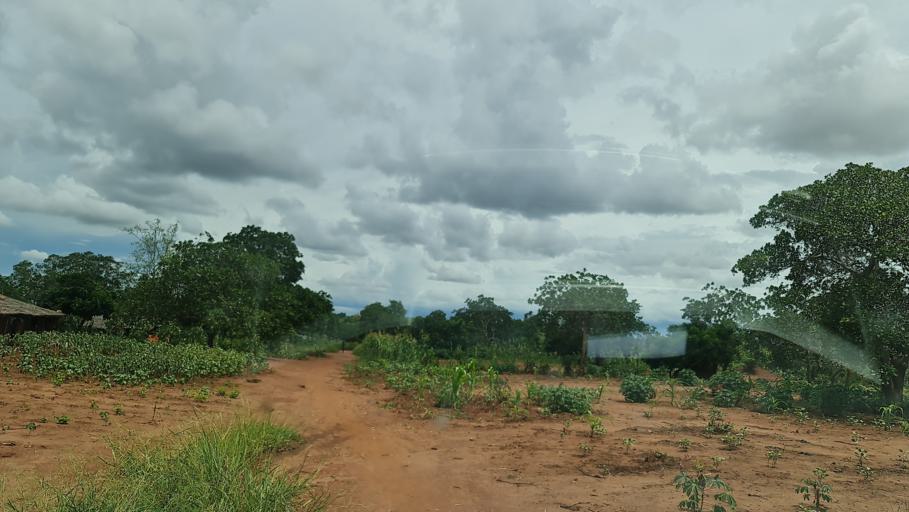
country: MZ
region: Nampula
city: Nacala
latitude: -14.7797
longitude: 39.9959
